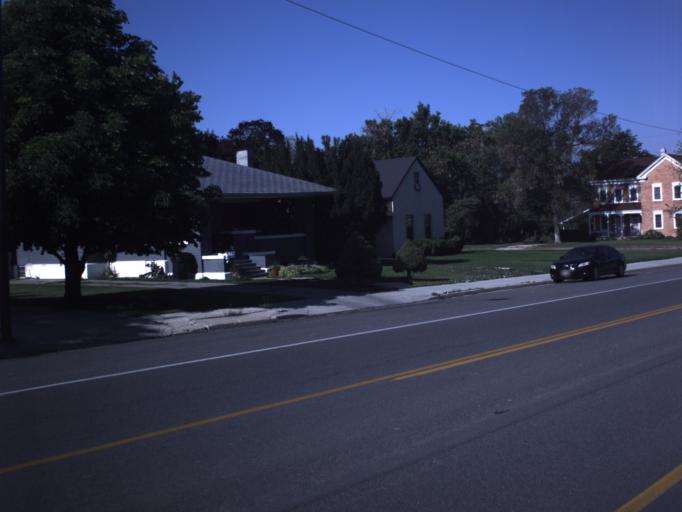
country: US
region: Utah
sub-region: Sanpete County
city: Mount Pleasant
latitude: 39.5468
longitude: -111.4620
